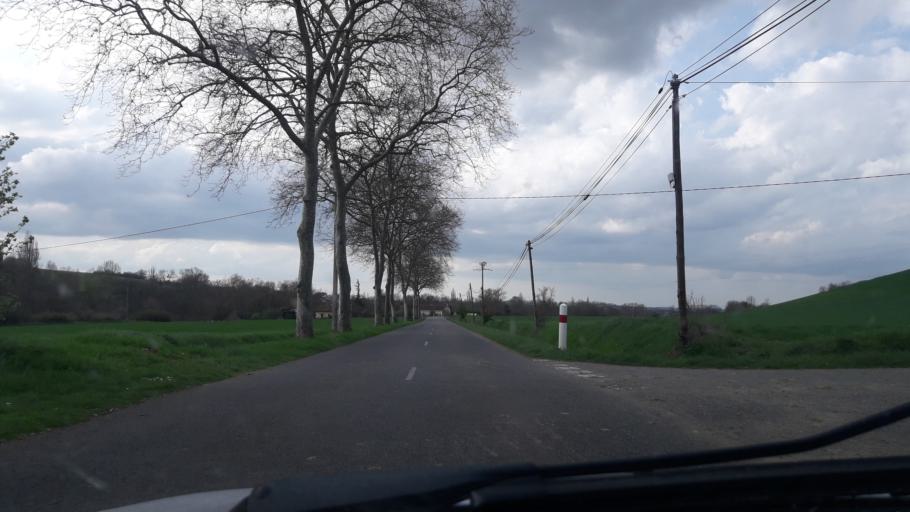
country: FR
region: Midi-Pyrenees
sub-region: Departement de la Haute-Garonne
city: Rieux-Volvestre
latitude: 43.2618
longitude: 1.2233
